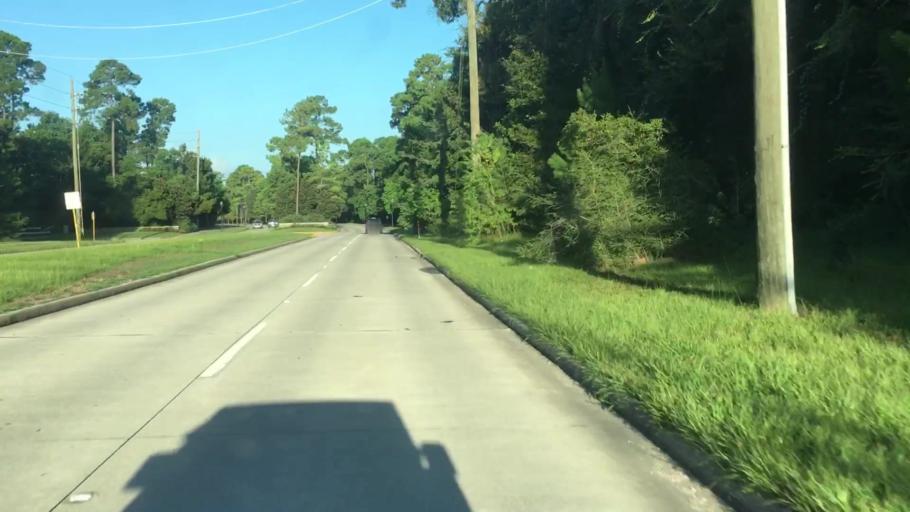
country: US
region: Texas
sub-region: Harris County
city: Atascocita
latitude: 29.9809
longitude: -95.1771
